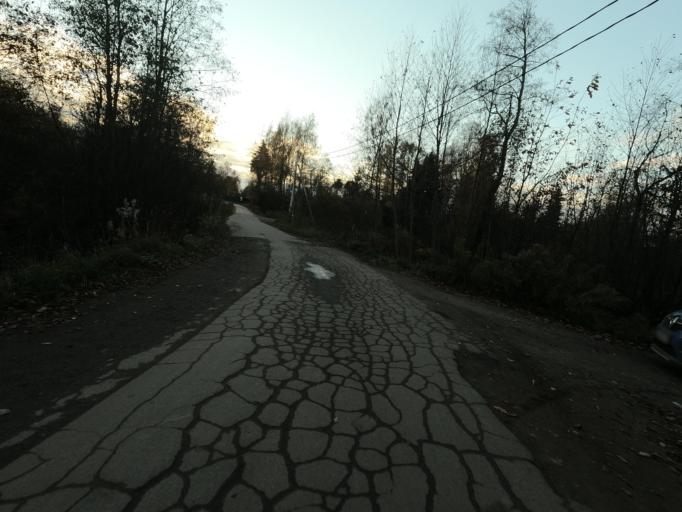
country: RU
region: Leningrad
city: Mga
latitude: 59.7814
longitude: 31.2015
